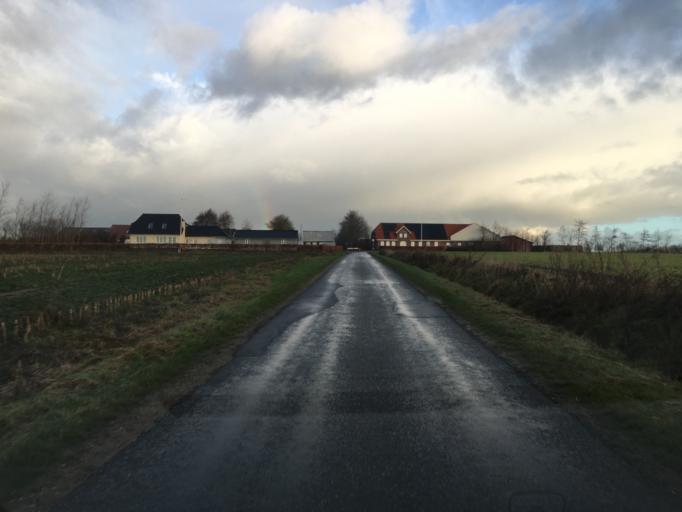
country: DK
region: South Denmark
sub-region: Tonder Kommune
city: Sherrebek
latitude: 55.1543
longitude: 8.8263
